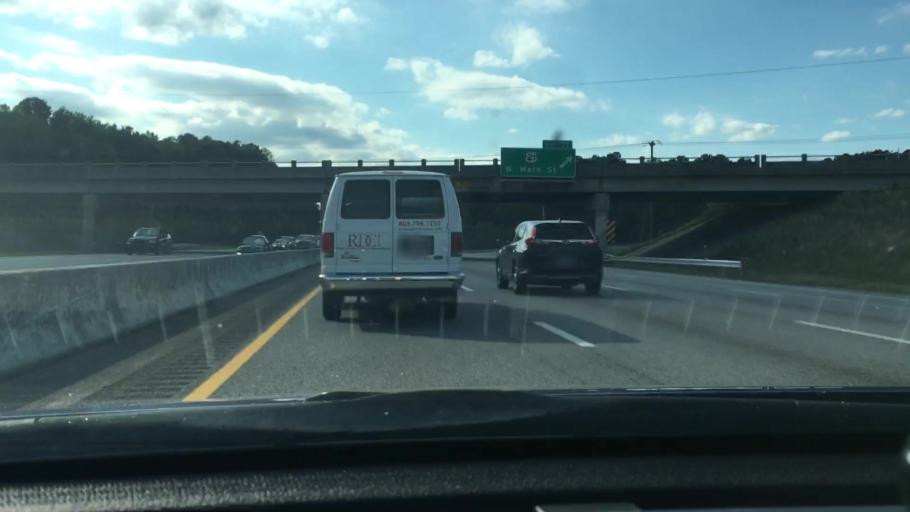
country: US
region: South Carolina
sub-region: Richland County
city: Dentsville
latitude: 34.0737
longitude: -80.9988
